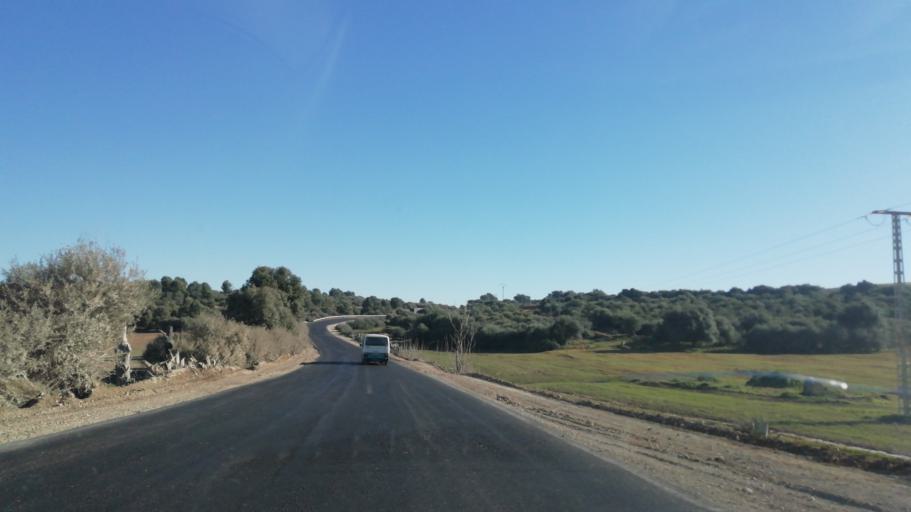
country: DZ
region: Relizane
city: Smala
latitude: 35.6682
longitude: 0.8082
